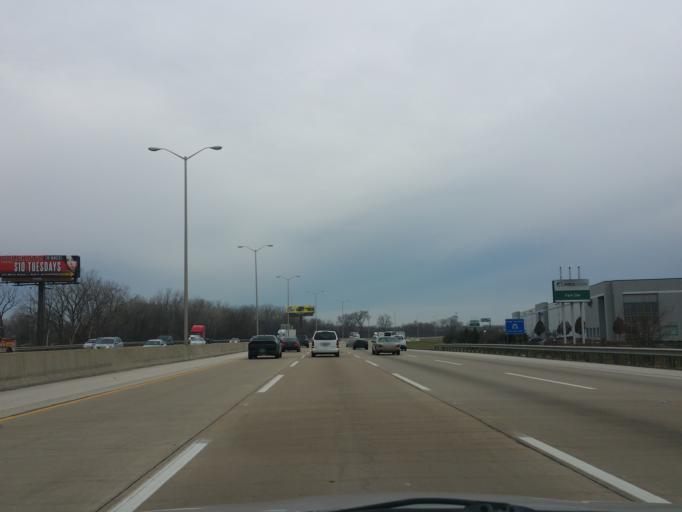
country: US
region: Illinois
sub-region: Cook County
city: Crestwood
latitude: 41.6746
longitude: -87.7687
